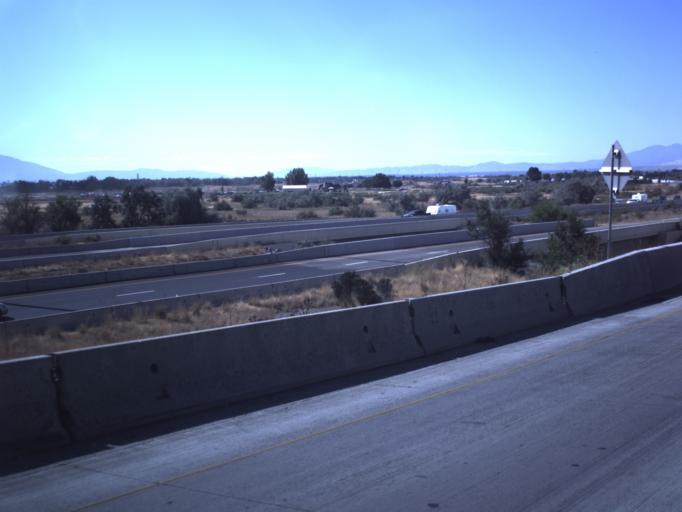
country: US
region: Utah
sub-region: Davis County
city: North Salt Lake
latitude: 40.8329
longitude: -111.9441
